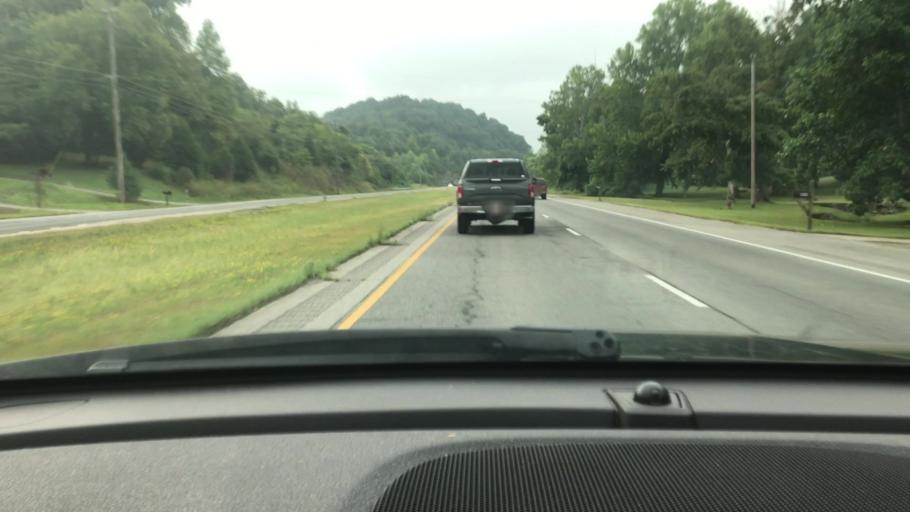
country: US
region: Tennessee
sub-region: Cheatham County
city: Ashland City
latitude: 36.2394
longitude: -87.0222
